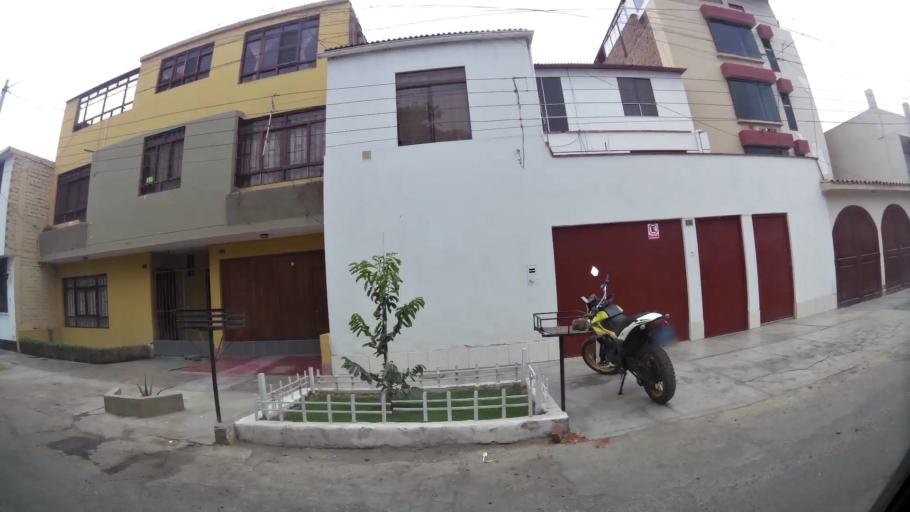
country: PE
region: La Libertad
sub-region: Provincia de Trujillo
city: Buenos Aires
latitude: -8.1315
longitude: -79.0421
